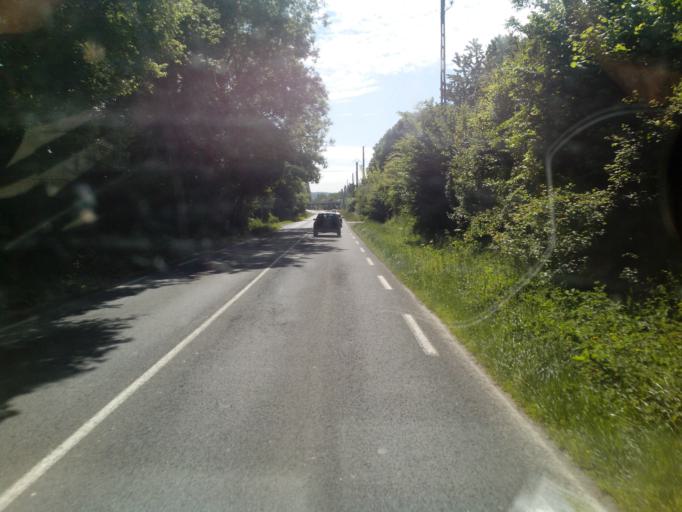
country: FR
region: Lower Normandy
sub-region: Departement du Calvados
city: Saint-Gatien-des-Bois
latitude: 49.2966
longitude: 0.2036
